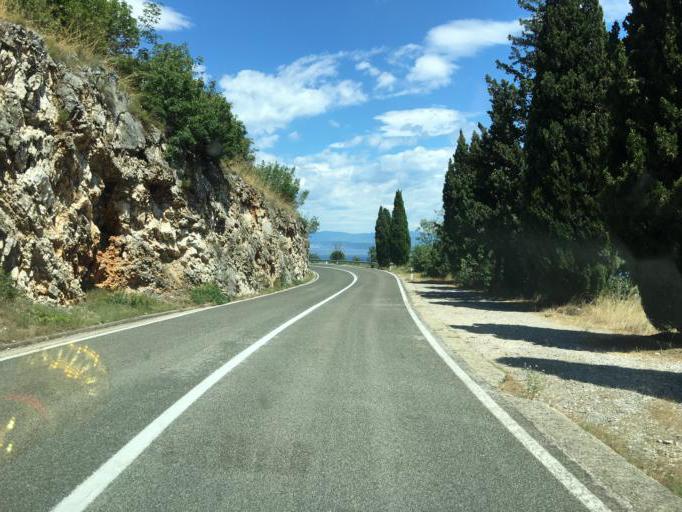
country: HR
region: Istarska
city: Lovran
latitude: 45.2013
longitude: 14.2401
